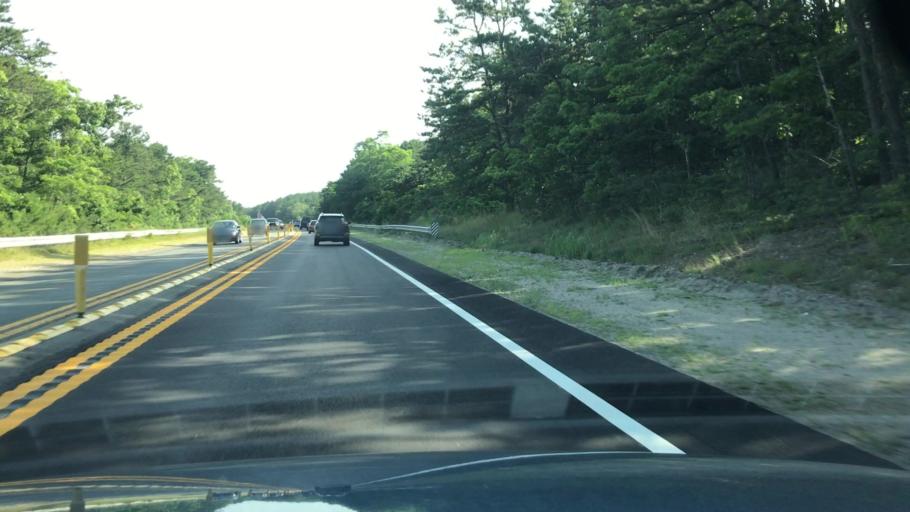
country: US
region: Massachusetts
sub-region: Barnstable County
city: Orleans
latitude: 41.7519
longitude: -70.0024
